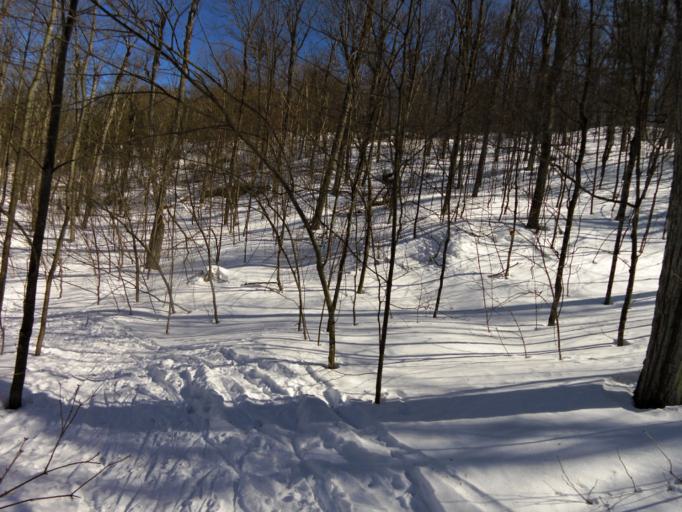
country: CA
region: Quebec
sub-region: Outaouais
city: Wakefield
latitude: 45.5139
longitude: -75.8622
